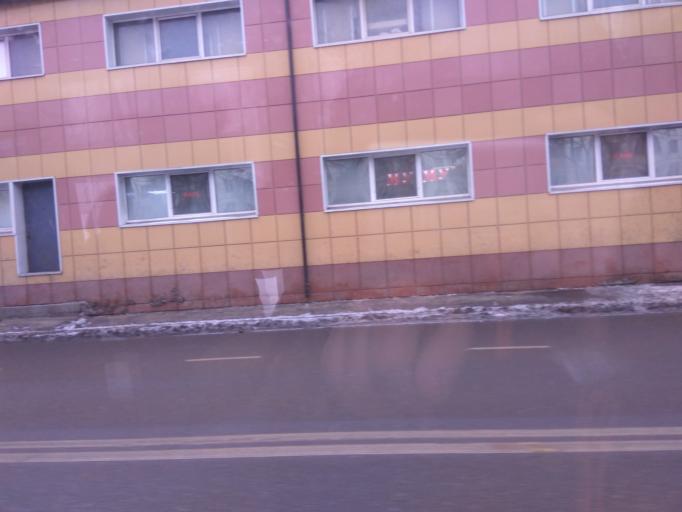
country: RU
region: Moscow
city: Metrogorodok
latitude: 55.8092
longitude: 37.7986
